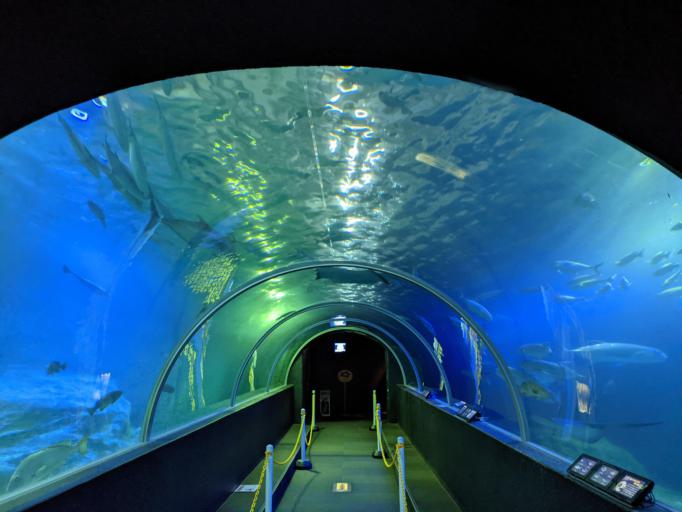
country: JP
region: Wakayama
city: Shingu
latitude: 33.4808
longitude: 135.7451
